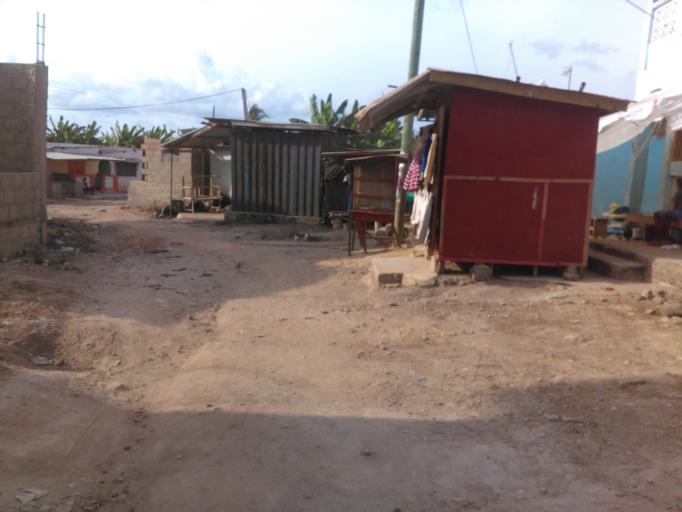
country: GH
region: Central
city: Cape Coast
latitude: 5.1112
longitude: -1.2967
